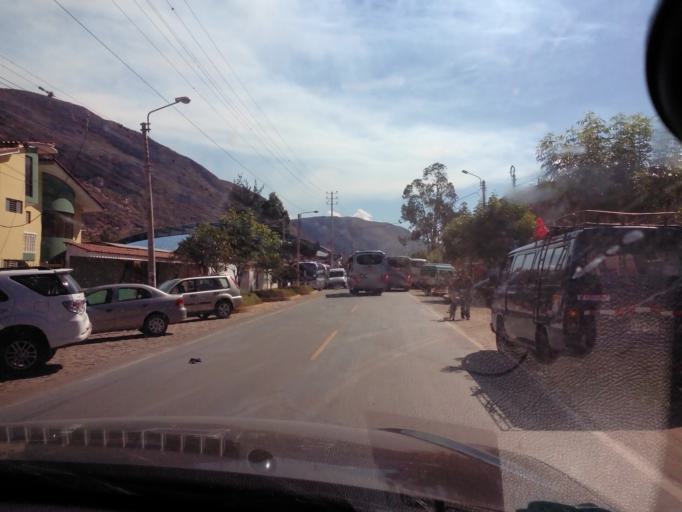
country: PE
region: Cusco
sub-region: Provincia de Urubamba
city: Urubamba
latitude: -13.3102
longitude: -72.1123
